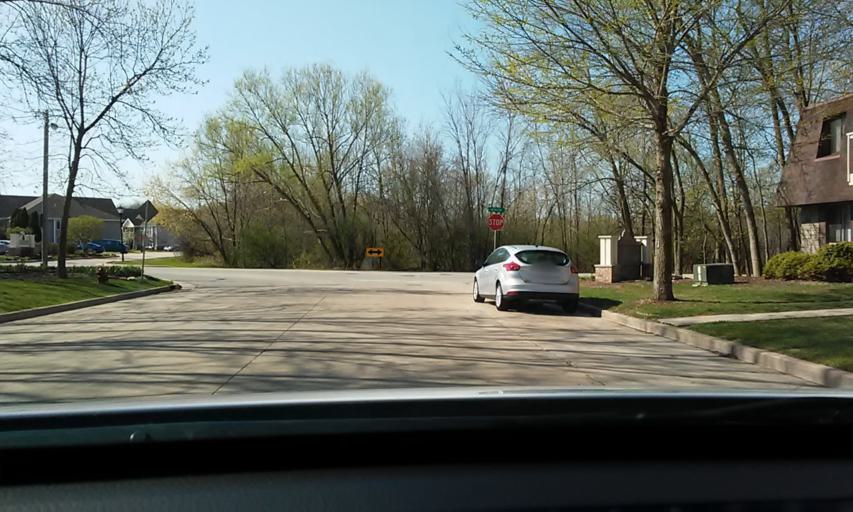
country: US
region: Wisconsin
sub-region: Milwaukee County
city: Hales Corners
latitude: 42.9812
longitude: -88.0536
